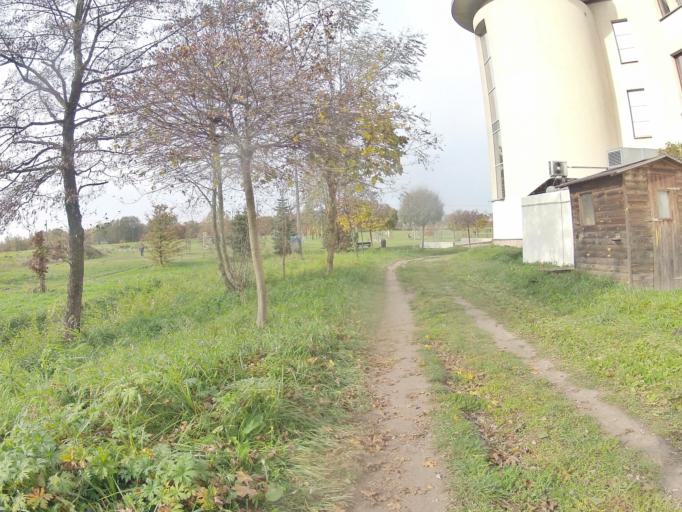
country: PL
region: Lesser Poland Voivodeship
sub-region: Krakow
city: Sidzina
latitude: 50.0256
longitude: 19.9003
